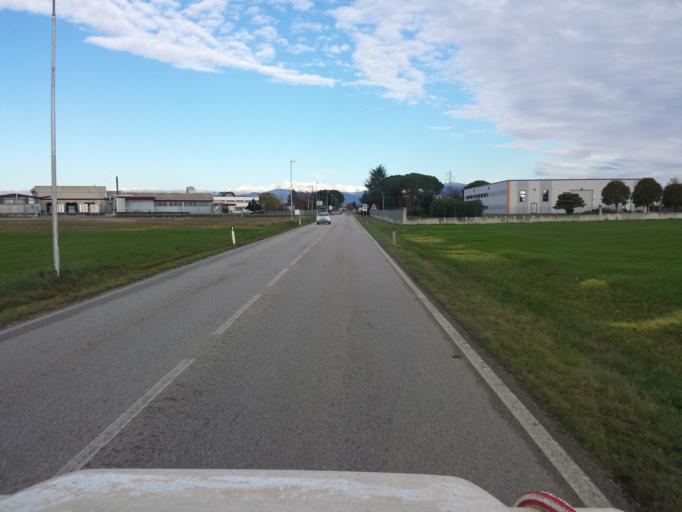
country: IT
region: Friuli Venezia Giulia
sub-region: Provincia di Udine
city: Chiopris
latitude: 45.9363
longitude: 13.3906
